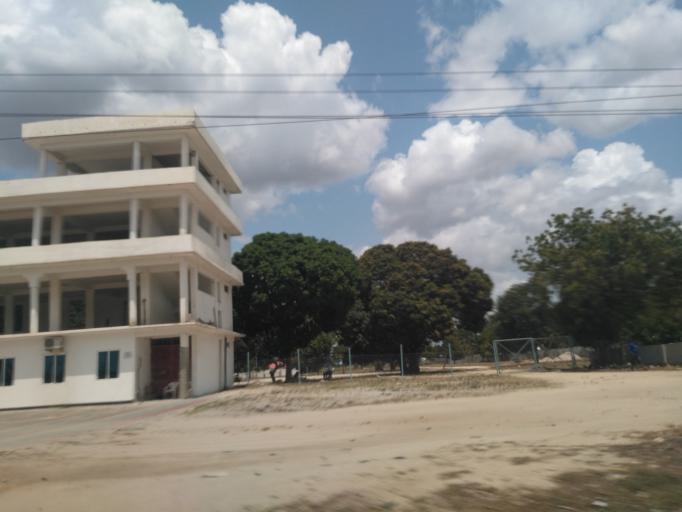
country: TZ
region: Dar es Salaam
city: Dar es Salaam
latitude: -6.8788
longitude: 39.3422
